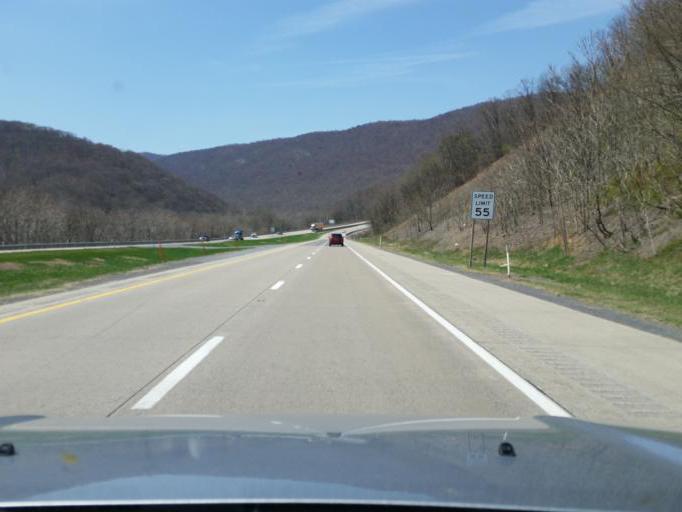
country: US
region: Pennsylvania
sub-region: Juniata County
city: Mifflintown
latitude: 40.6058
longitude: -77.4309
